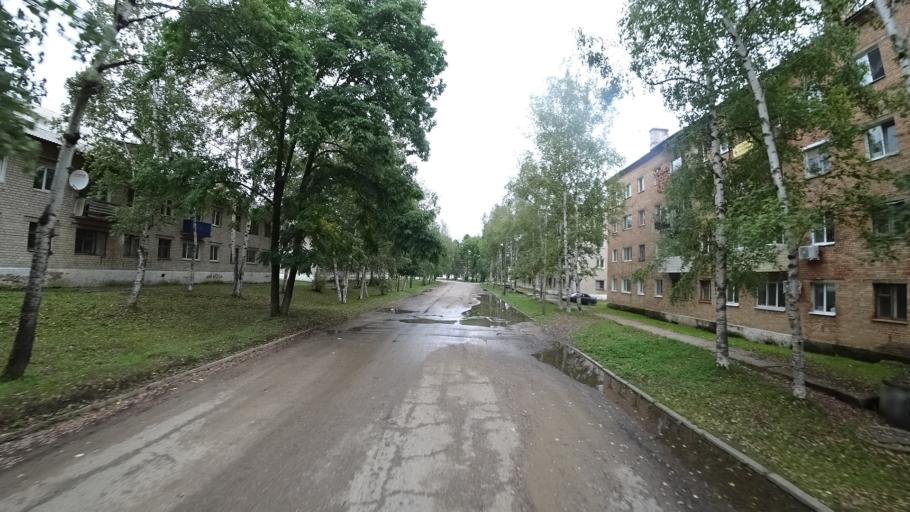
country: RU
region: Primorskiy
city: Rettikhovka
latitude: 44.1684
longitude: 132.7750
